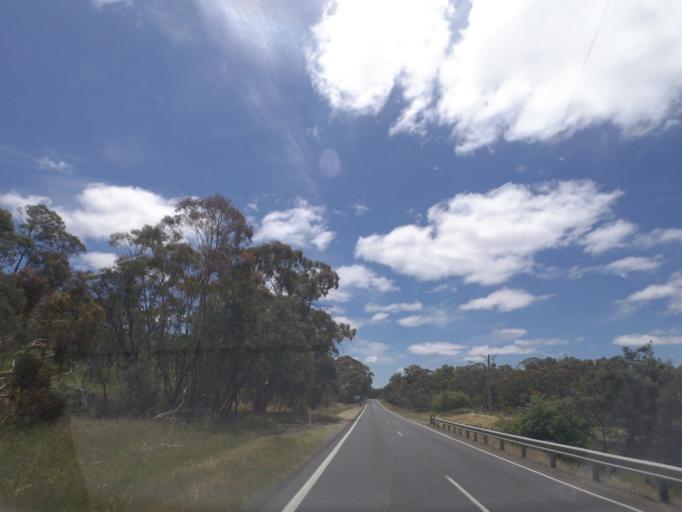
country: AU
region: Victoria
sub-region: Mount Alexander
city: Castlemaine
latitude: -37.2951
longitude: 144.1628
